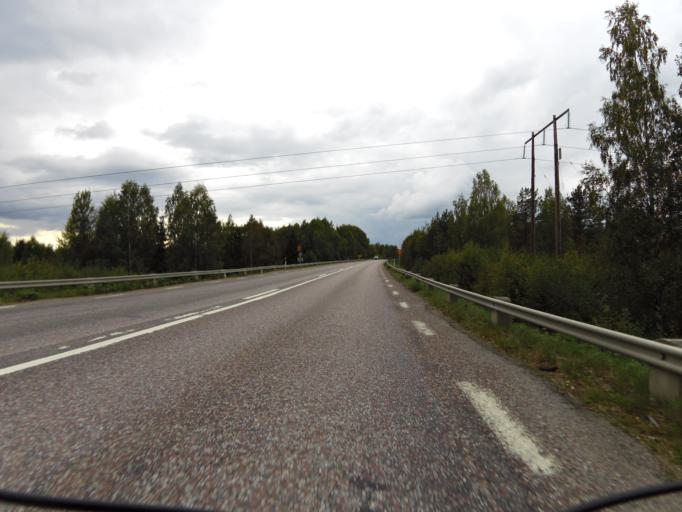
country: SE
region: Gaevleborg
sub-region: Ockelbo Kommun
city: Ockelbo
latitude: 60.9042
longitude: 16.7339
